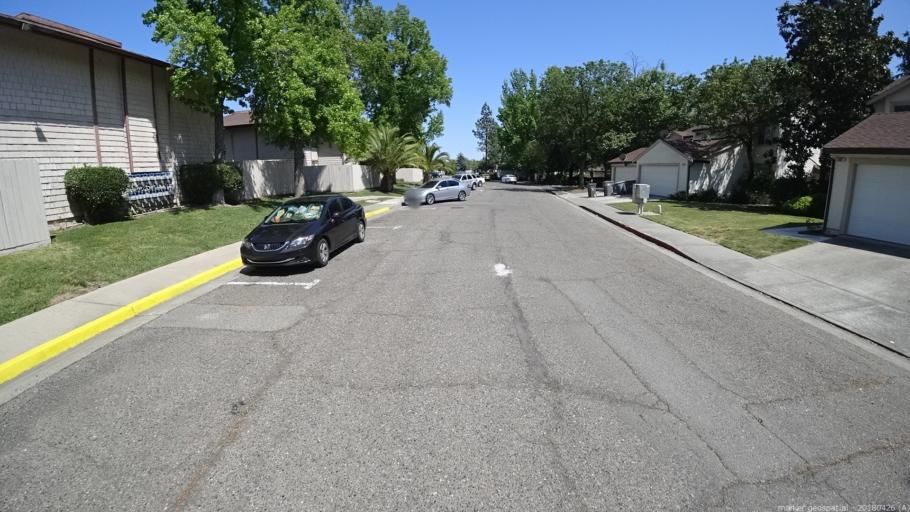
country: US
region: California
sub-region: Yolo County
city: West Sacramento
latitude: 38.5515
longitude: -121.5407
